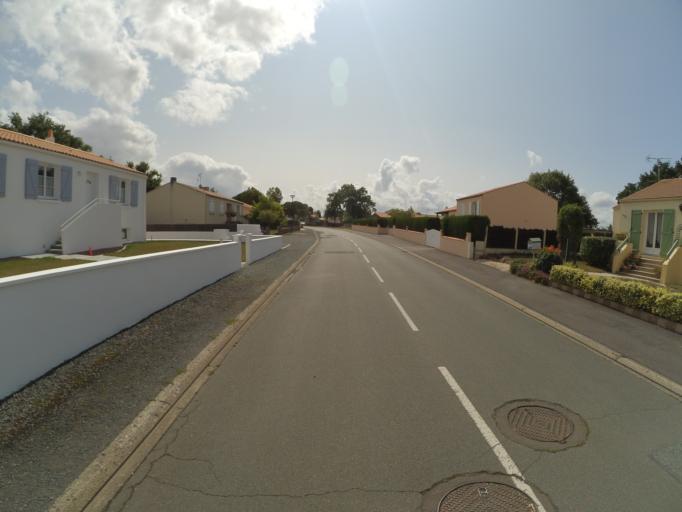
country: FR
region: Pays de la Loire
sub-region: Departement de la Vendee
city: Saint-Hilaire-de-Loulay
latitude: 47.0001
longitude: -1.3265
